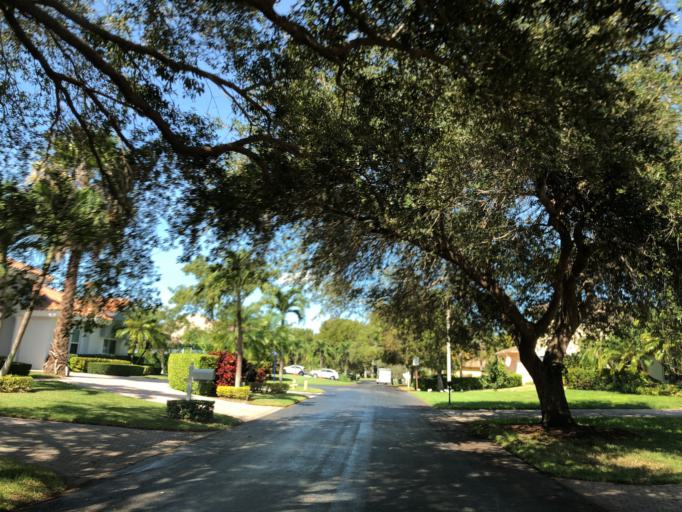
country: US
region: Florida
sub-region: Miami-Dade County
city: Palmetto Bay
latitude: 25.6159
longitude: -80.3304
